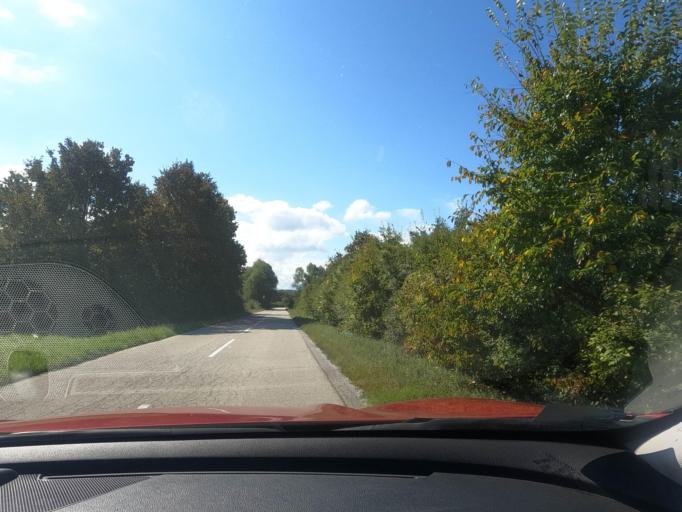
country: BA
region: Federation of Bosnia and Herzegovina
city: Vrnograc
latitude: 45.2551
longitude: 15.9454
